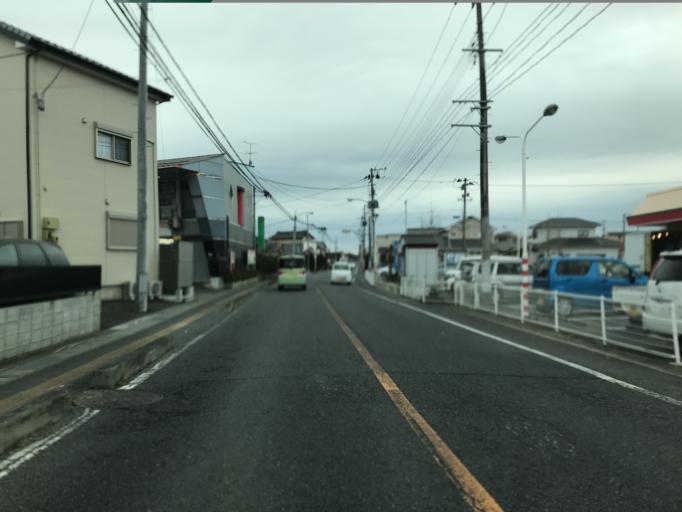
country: JP
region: Fukushima
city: Iwaki
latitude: 37.0827
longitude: 140.8786
